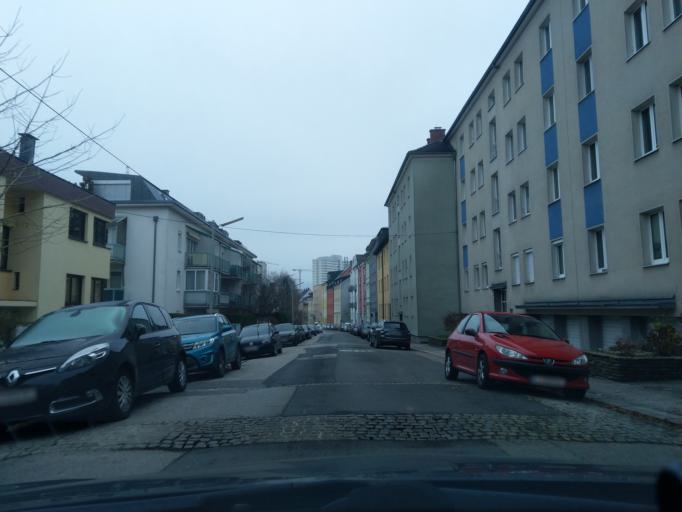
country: AT
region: Upper Austria
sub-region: Linz Stadt
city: Linz
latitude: 48.3155
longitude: 14.2752
